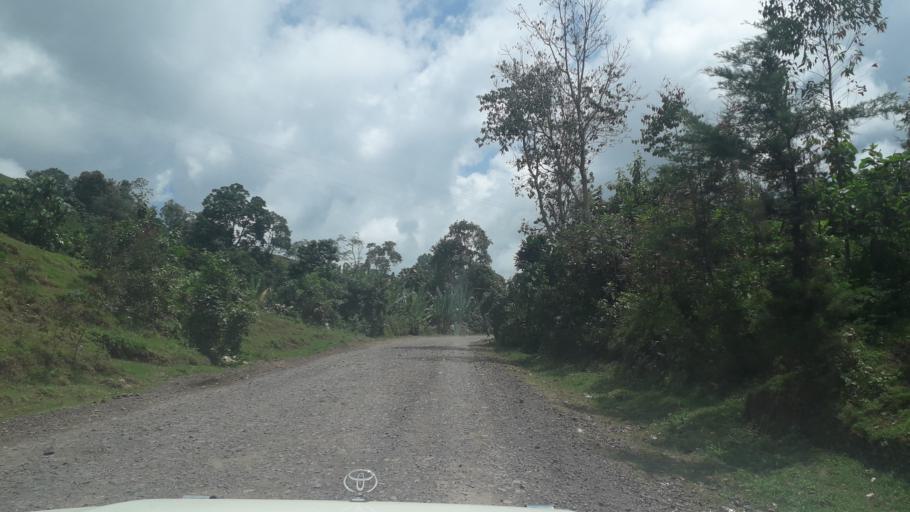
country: ET
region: Oromiya
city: Jima
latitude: 7.4306
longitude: 36.8737
